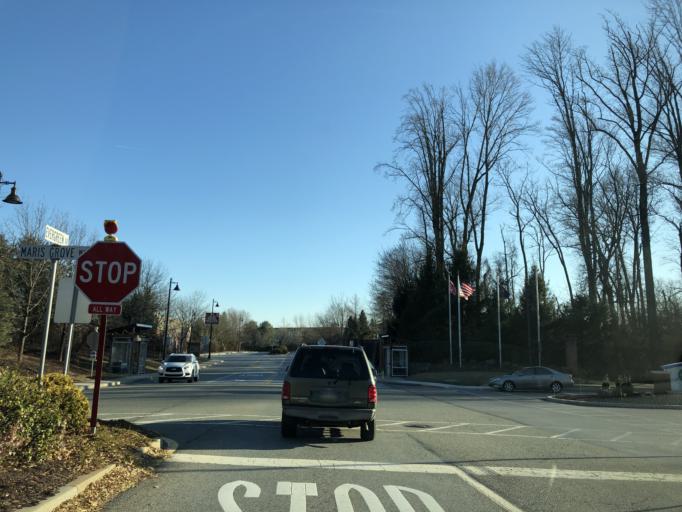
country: US
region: Pennsylvania
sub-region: Delaware County
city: Chester Heights
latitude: 39.8812
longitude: -75.5295
